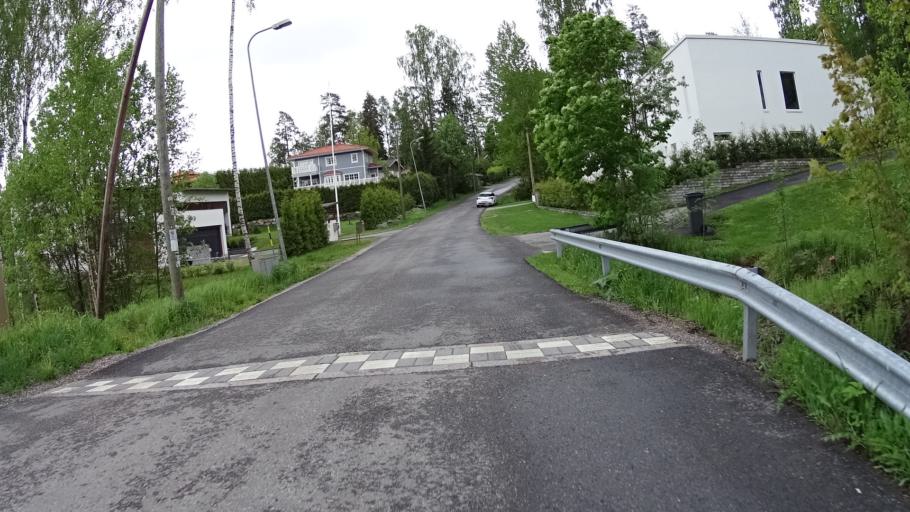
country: FI
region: Uusimaa
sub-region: Helsinki
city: Kauniainen
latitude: 60.2215
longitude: 24.7232
